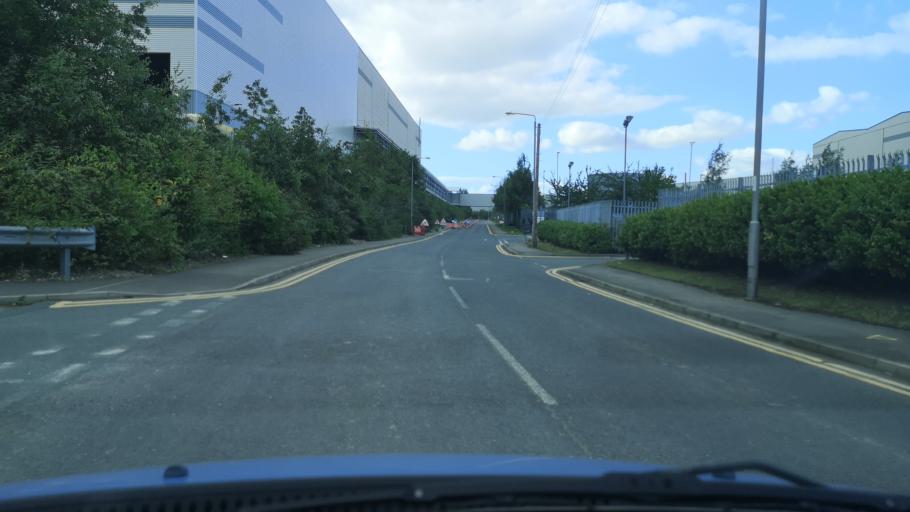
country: GB
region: England
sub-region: City and Borough of Wakefield
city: South Elmsall
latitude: 53.6007
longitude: -1.2679
